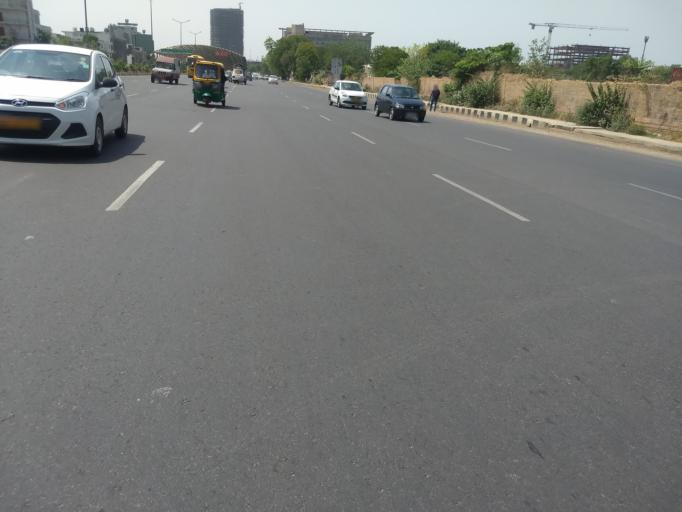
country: IN
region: Haryana
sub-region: Gurgaon
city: Gurgaon
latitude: 28.4651
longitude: 77.0628
